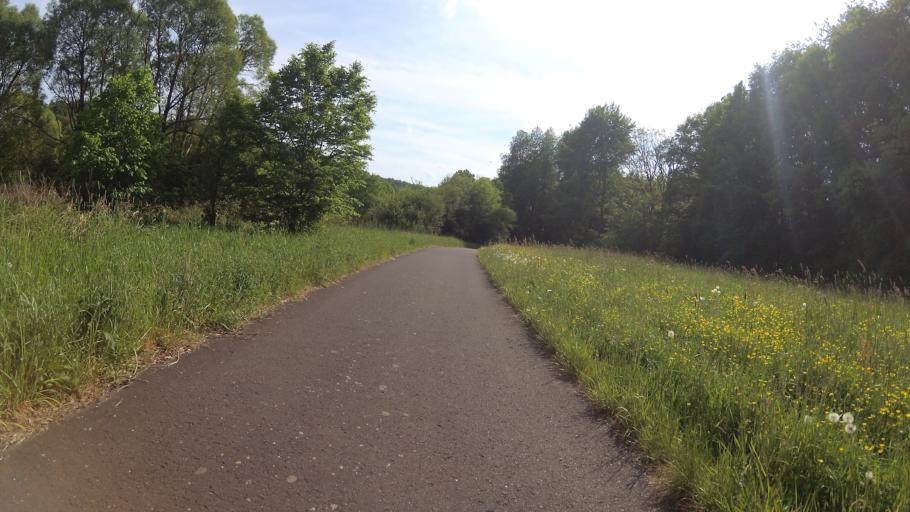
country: DE
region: Saarland
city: Sankt Wendel
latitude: 49.4414
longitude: 7.1435
